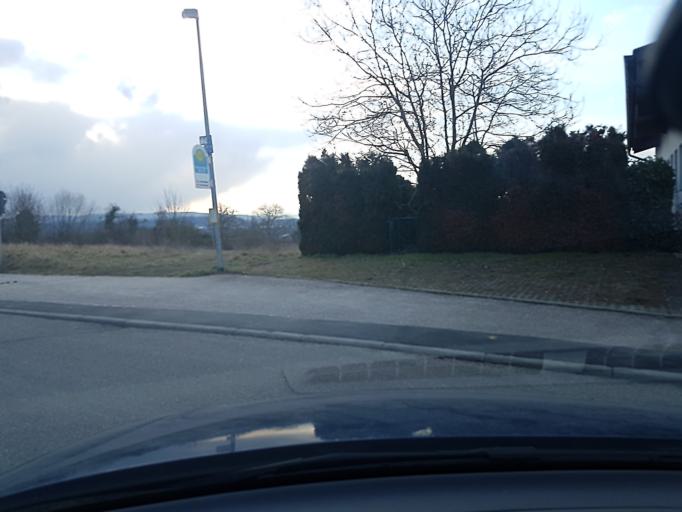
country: DE
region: Baden-Wuerttemberg
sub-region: Regierungsbezirk Stuttgart
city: Talheim
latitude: 49.0738
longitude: 9.1766
